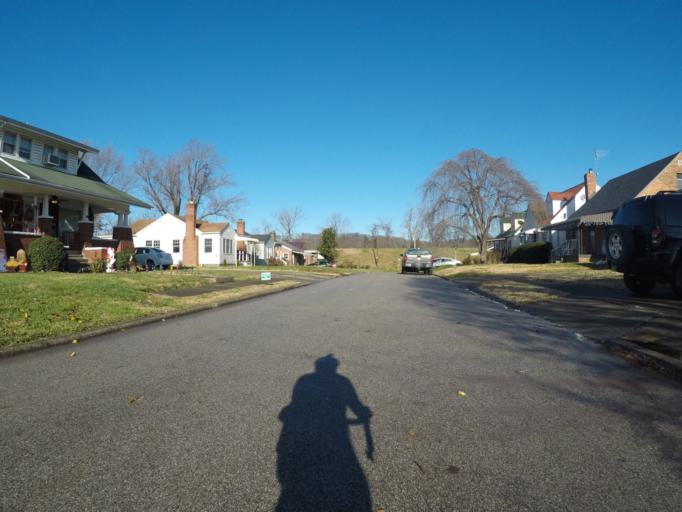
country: US
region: Ohio
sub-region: Lawrence County
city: Burlington
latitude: 38.4049
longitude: -82.5084
